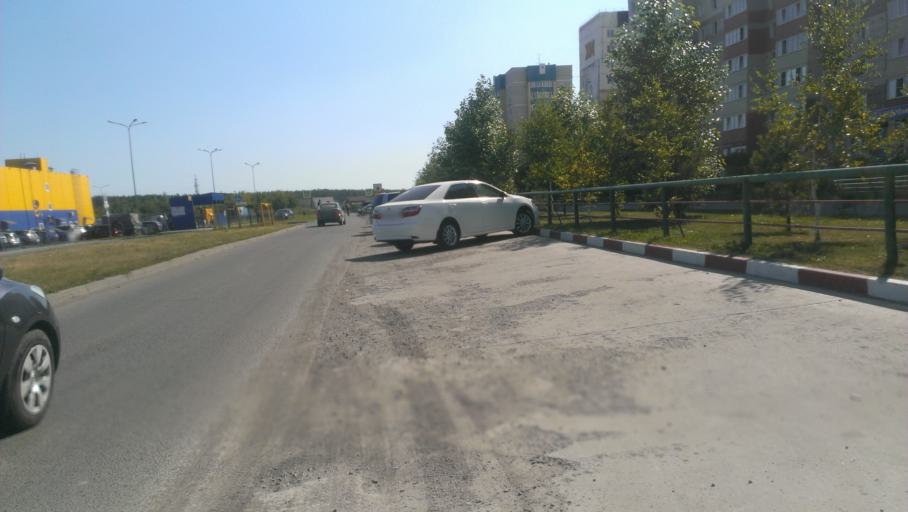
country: RU
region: Altai Krai
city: Novosilikatnyy
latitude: 53.3277
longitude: 83.6835
